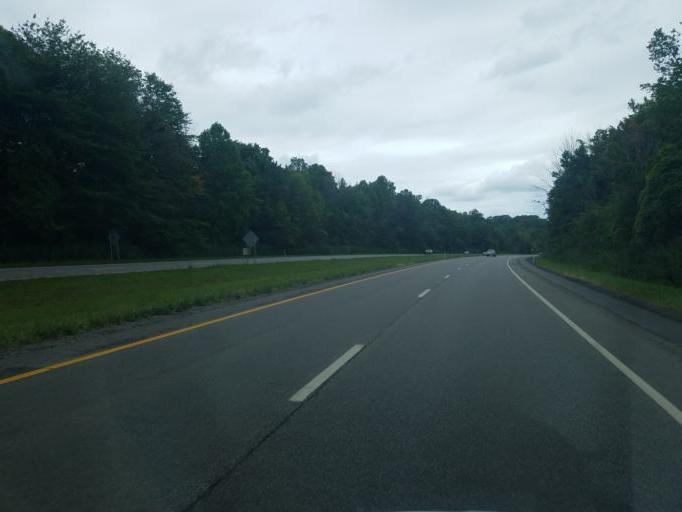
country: US
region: Ohio
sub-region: Lake County
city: Painesville
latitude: 41.6809
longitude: -81.2540
